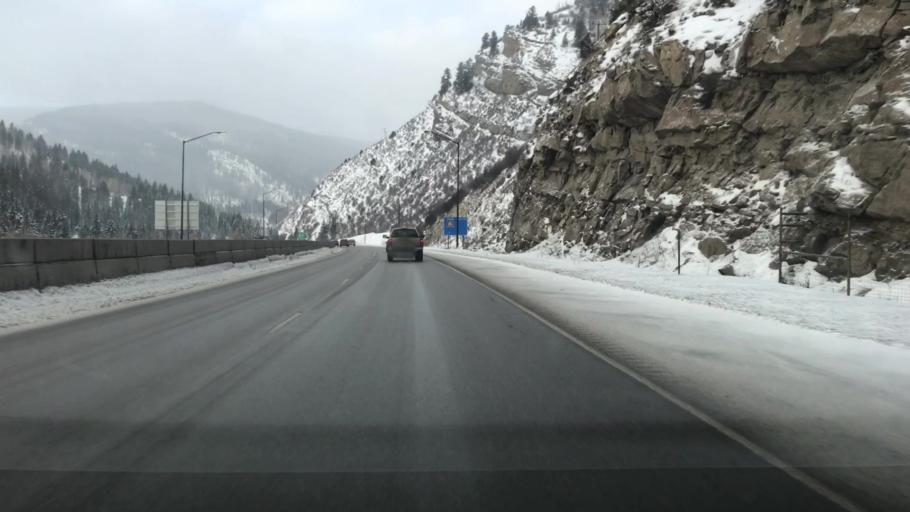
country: US
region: Colorado
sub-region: Eagle County
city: Minturn
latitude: 39.6198
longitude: -106.4322
